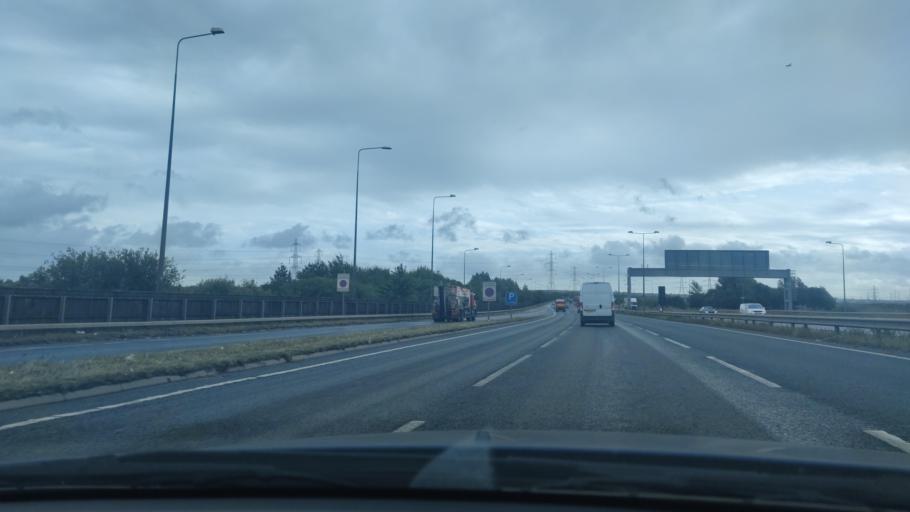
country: GB
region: England
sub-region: Greater London
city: Erith
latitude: 51.5110
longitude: 0.1888
